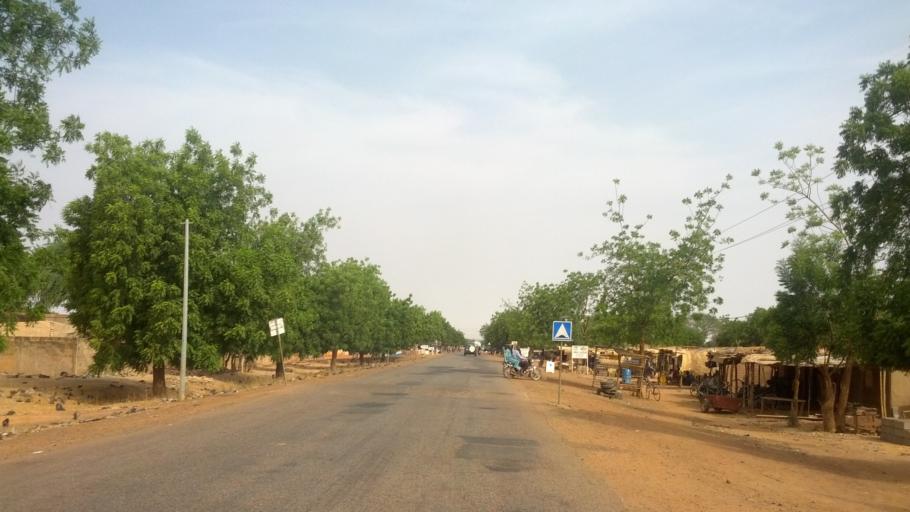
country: BF
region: Centre-Nord
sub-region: Province du Sanmatenga
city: Kaya
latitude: 12.9084
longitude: -1.0782
